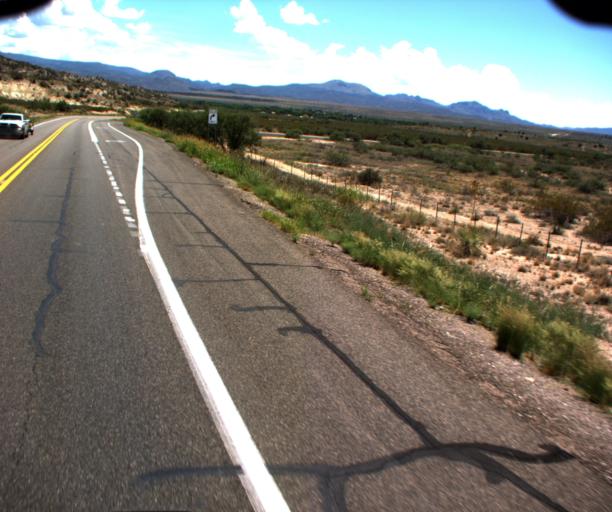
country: US
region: Arizona
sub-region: Yavapai County
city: Camp Verde
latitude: 34.5343
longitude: -111.8142
